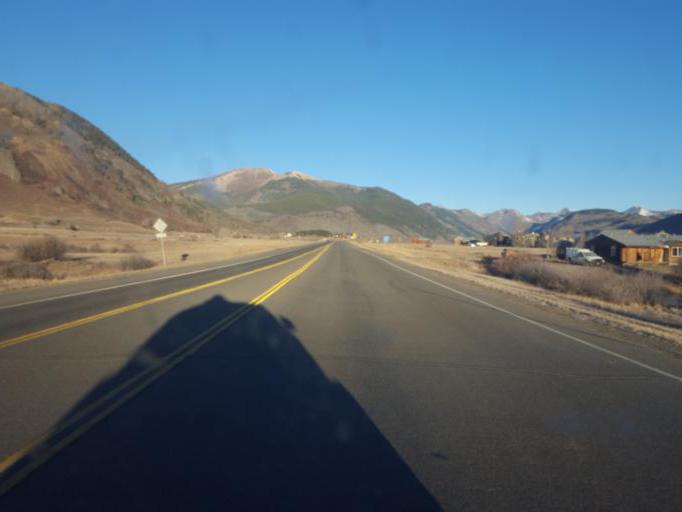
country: US
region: Colorado
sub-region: Gunnison County
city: Crested Butte
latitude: 38.8522
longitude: -106.9539
